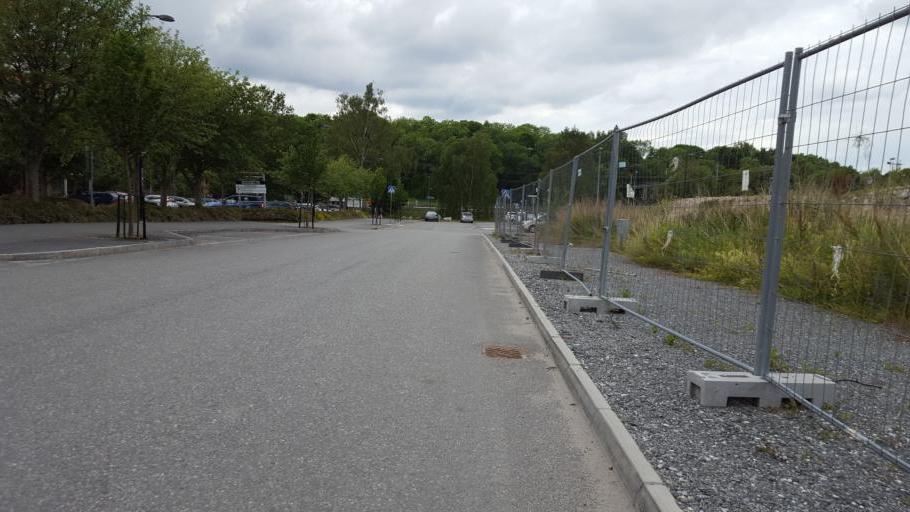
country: SE
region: Stockholm
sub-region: Upplands Vasby Kommun
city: Upplands Vaesby
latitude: 59.5182
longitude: 17.9002
